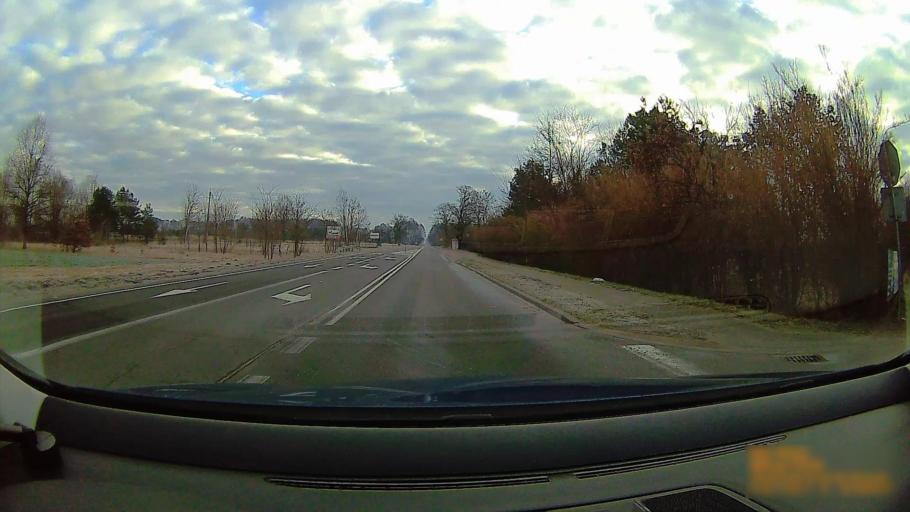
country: PL
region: Greater Poland Voivodeship
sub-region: Powiat koninski
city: Stare Miasto
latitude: 52.1986
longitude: 18.1631
